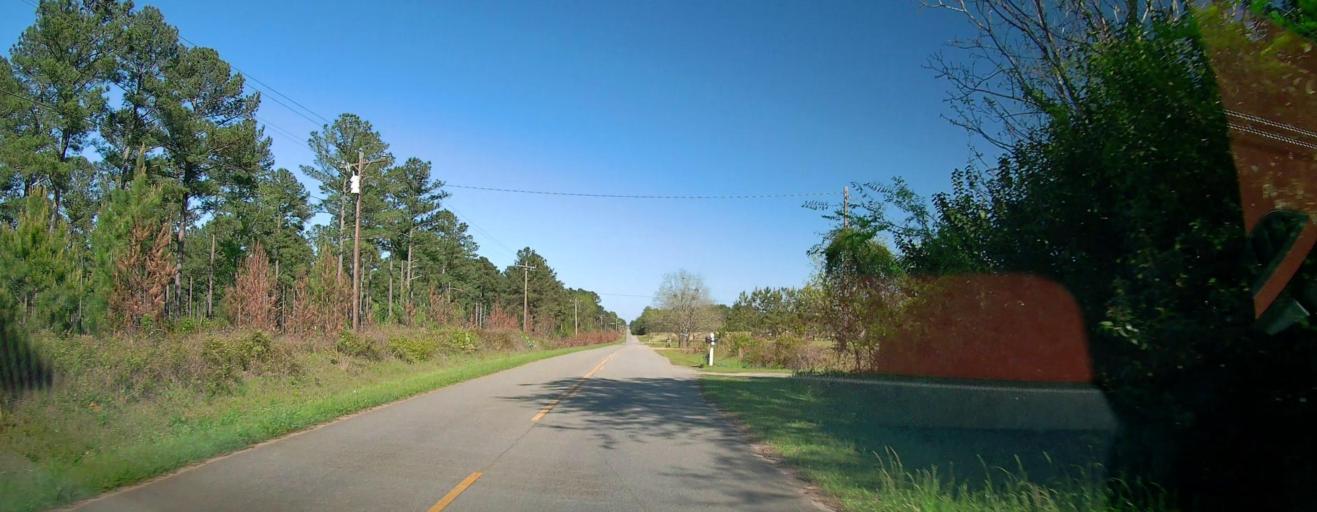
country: US
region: Georgia
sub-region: Pulaski County
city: Hawkinsville
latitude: 32.2406
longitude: -83.5478
